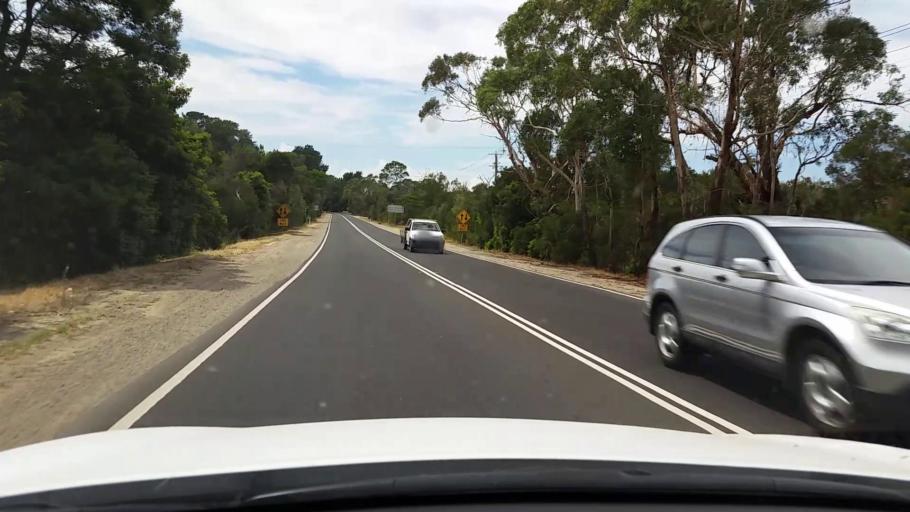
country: AU
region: Victoria
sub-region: Mornington Peninsula
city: Mount Martha
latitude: -38.2822
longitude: 145.0689
